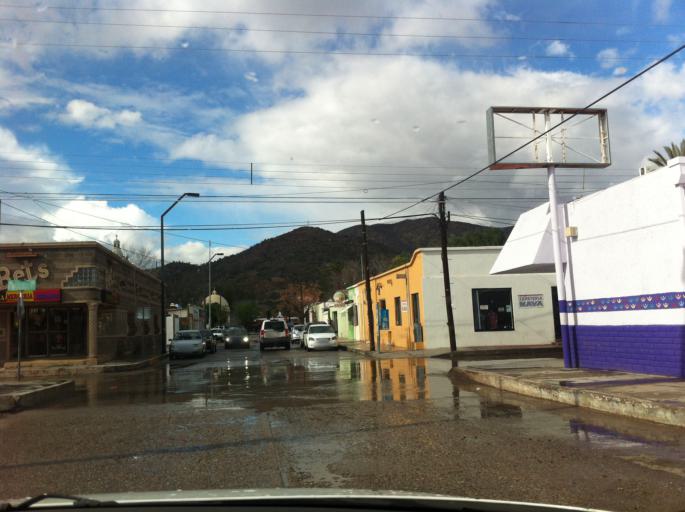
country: MX
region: Sonora
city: Magdalena de Kino
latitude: 30.6290
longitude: -110.9719
